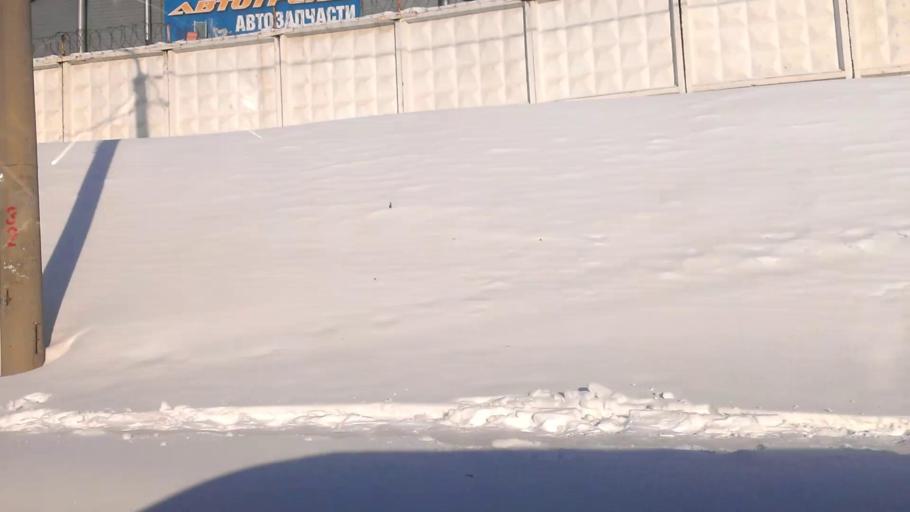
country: RU
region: Altai Krai
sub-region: Gorod Barnaulskiy
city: Barnaul
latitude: 53.3401
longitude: 83.7420
